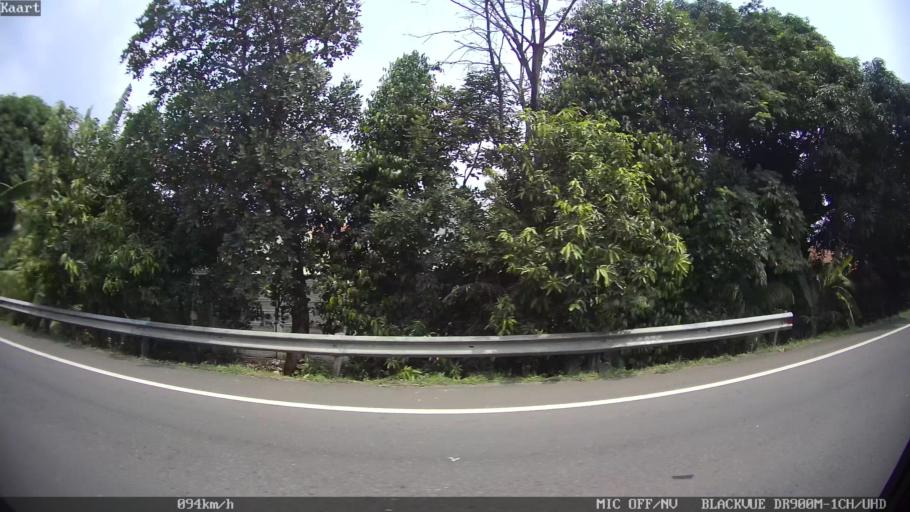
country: ID
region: Banten
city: Curug
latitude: -5.9823
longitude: 106.0277
